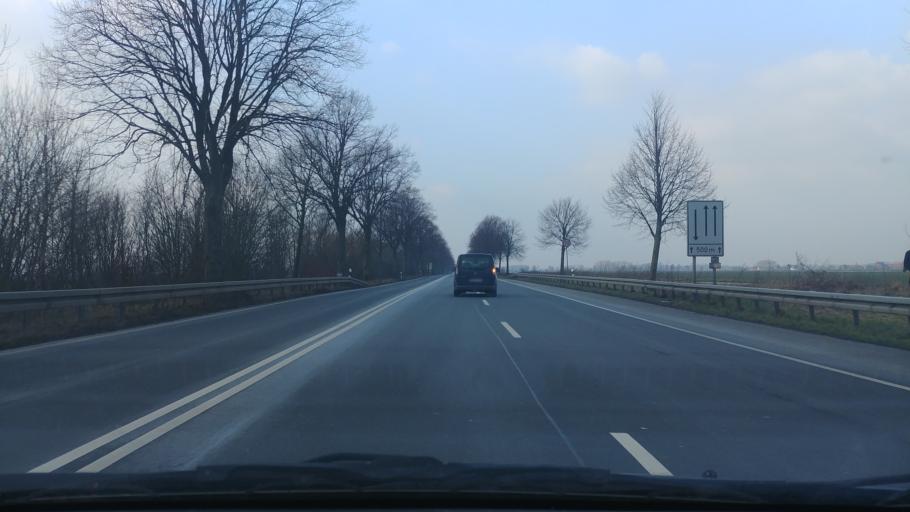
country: DE
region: Lower Saxony
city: Pattensen
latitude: 52.2780
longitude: 9.7592
